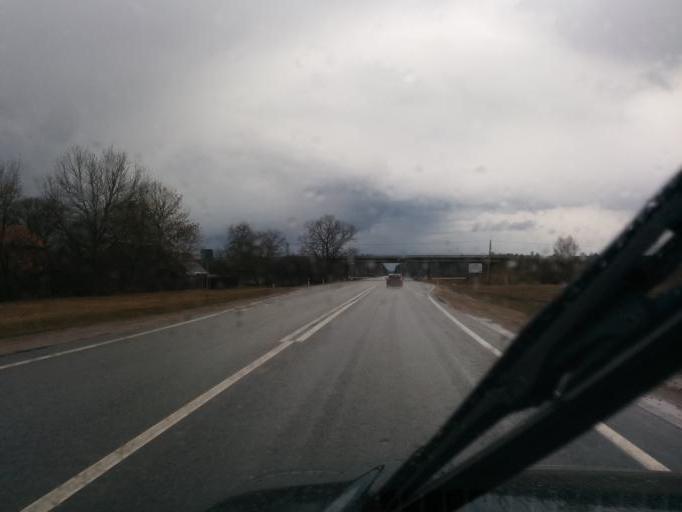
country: LV
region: Babite
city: Pinki
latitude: 56.8764
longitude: 23.9556
